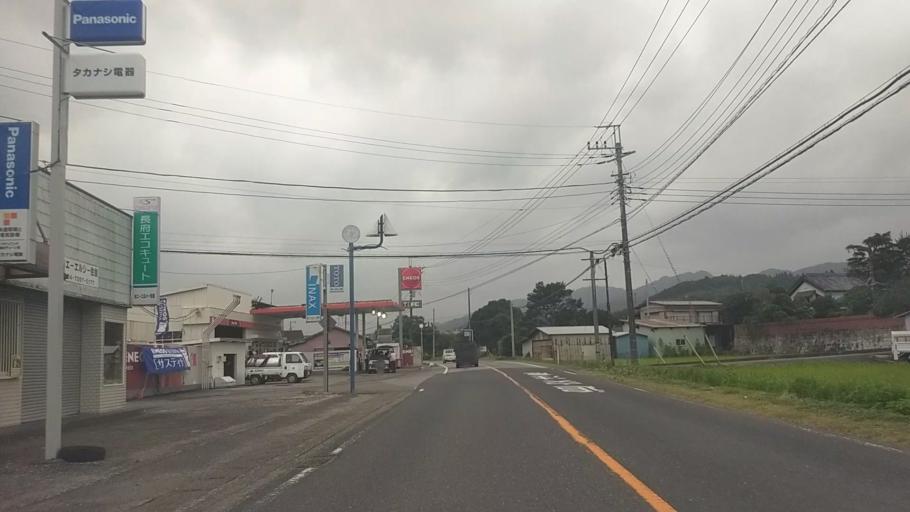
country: JP
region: Chiba
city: Kawaguchi
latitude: 35.1349
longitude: 140.0033
